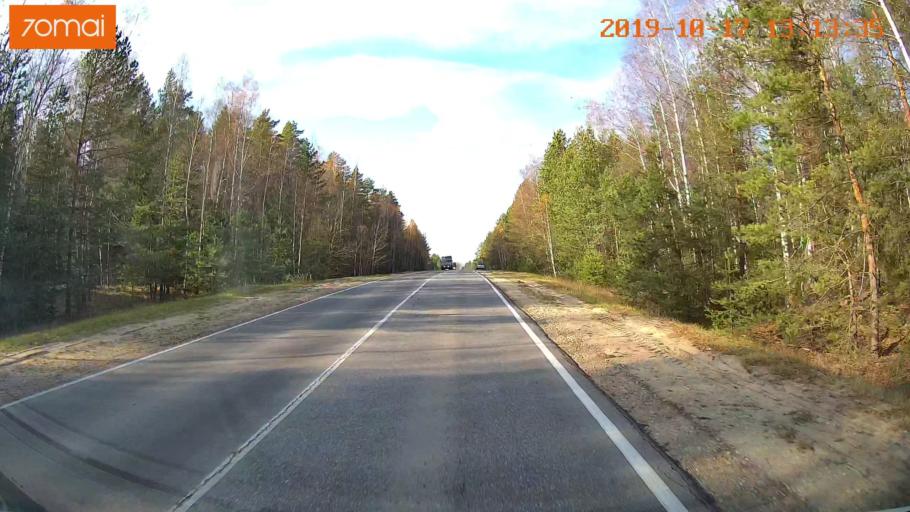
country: RU
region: Rjazan
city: Gus'-Zheleznyy
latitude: 55.0462
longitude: 41.1881
